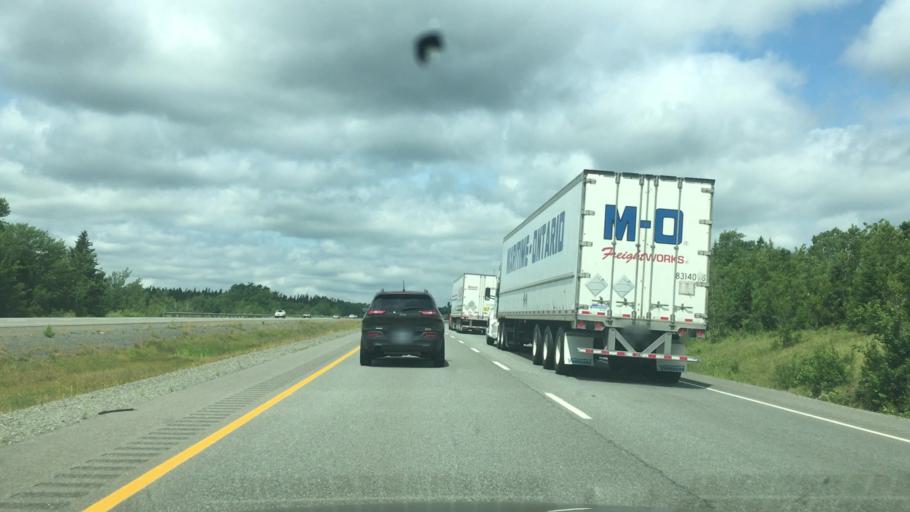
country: CA
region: Nova Scotia
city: Springhill
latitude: 45.7081
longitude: -64.0354
